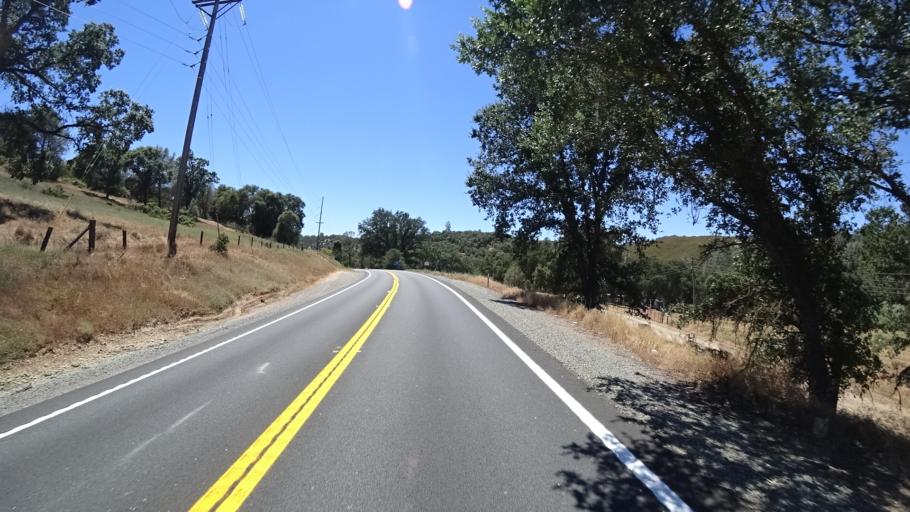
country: US
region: California
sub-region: Calaveras County
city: San Andreas
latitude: 38.2093
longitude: -120.7065
